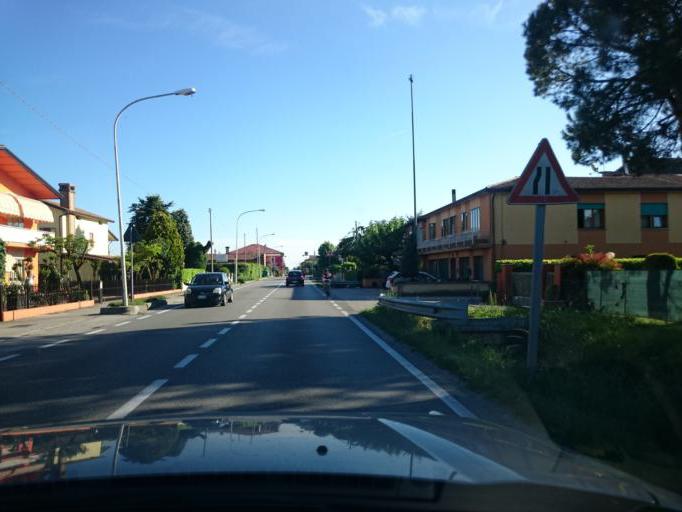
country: IT
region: Veneto
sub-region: Provincia di Venezia
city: Caselle
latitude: 45.5013
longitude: 12.0099
